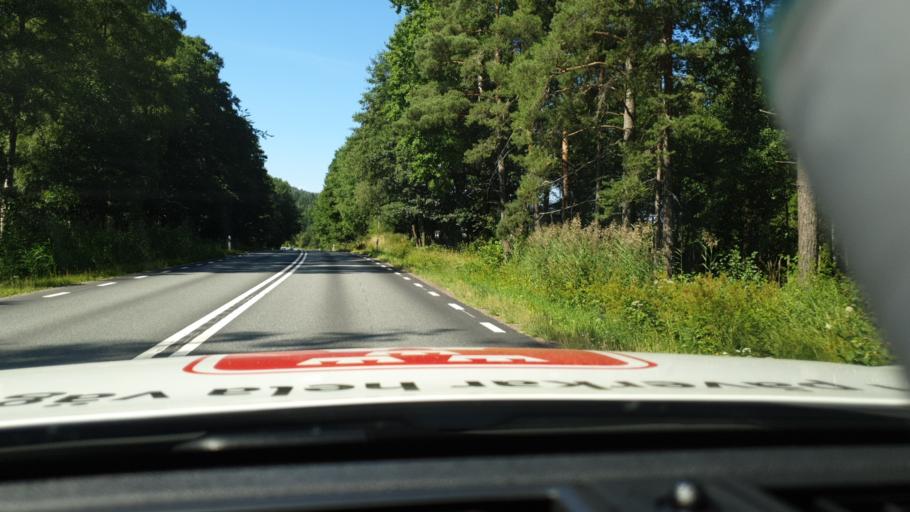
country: SE
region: Joenkoeping
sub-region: Jonkopings Kommun
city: Graenna
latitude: 58.0106
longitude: 14.5326
